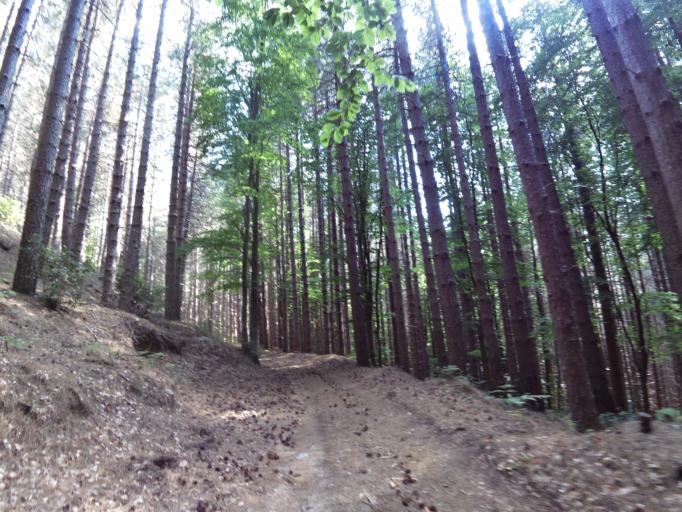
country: IT
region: Calabria
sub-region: Provincia di Vibo-Valentia
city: Nardodipace
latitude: 38.4880
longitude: 16.3815
